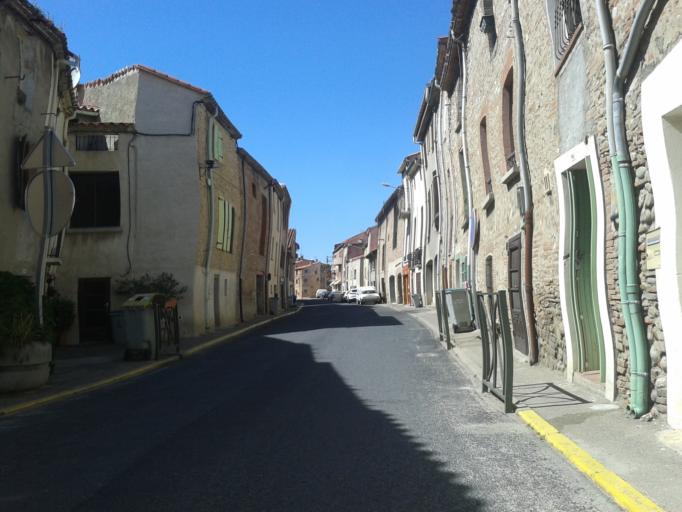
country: FR
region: Languedoc-Roussillon
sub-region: Departement des Pyrenees-Orientales
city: Corneilla-la-Riviere
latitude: 42.6980
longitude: 2.7297
